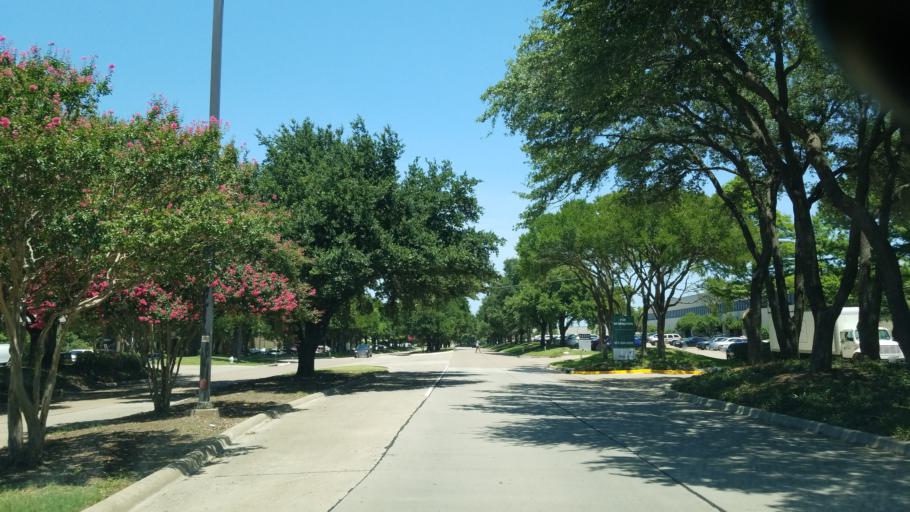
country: US
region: Texas
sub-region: Dallas County
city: Farmers Branch
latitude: 32.9301
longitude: -96.9065
